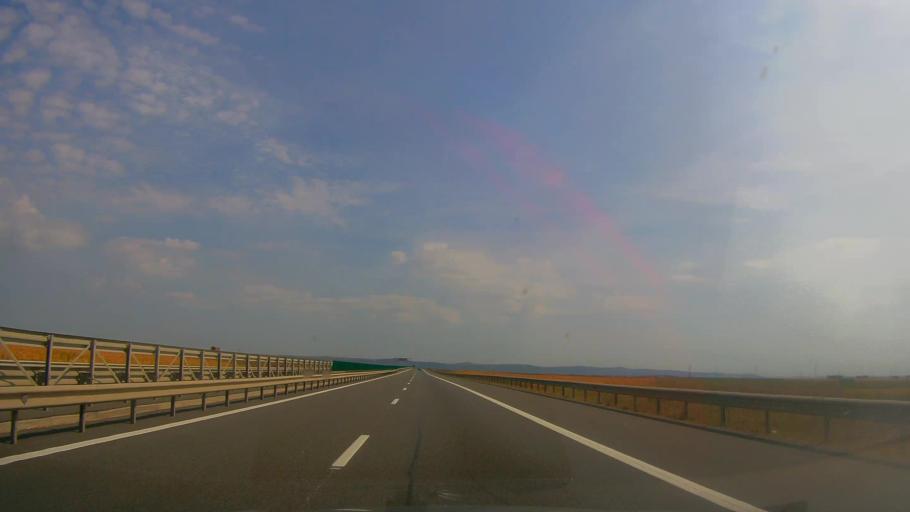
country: RO
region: Cluj
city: Turda
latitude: 46.5236
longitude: 23.8198
